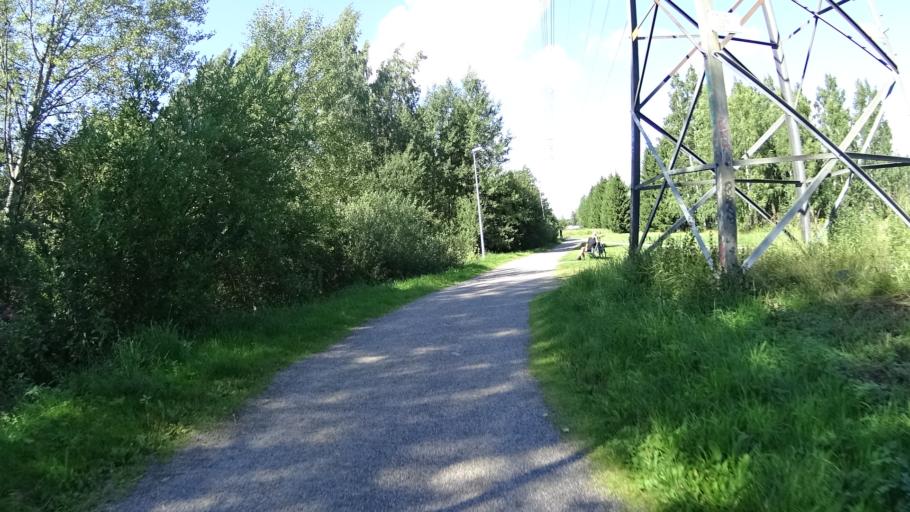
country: FI
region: Uusimaa
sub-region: Helsinki
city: Teekkarikylae
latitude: 60.2317
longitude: 24.8697
